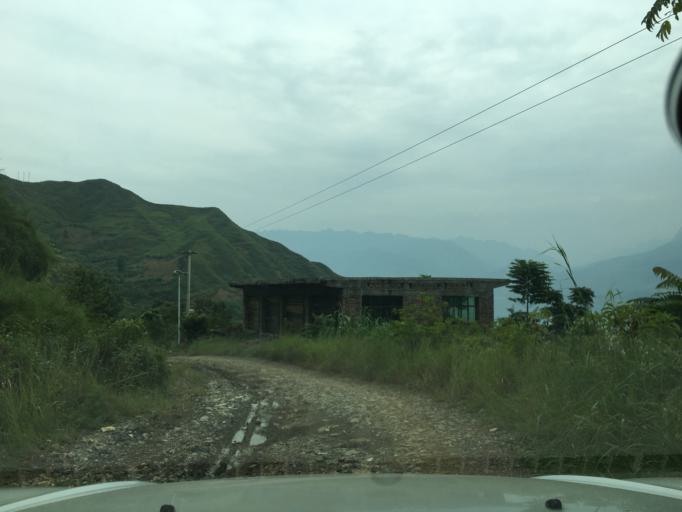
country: CN
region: Guizhou Sheng
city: Liupanshui
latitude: 26.0363
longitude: 105.1869
